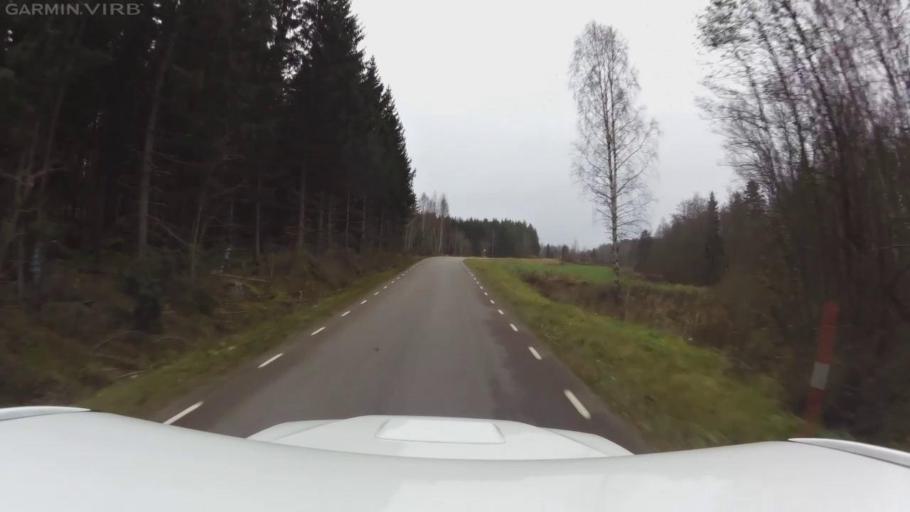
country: SE
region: OEstergoetland
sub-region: Linkopings Kommun
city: Vikingstad
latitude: 58.2273
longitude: 15.3956
